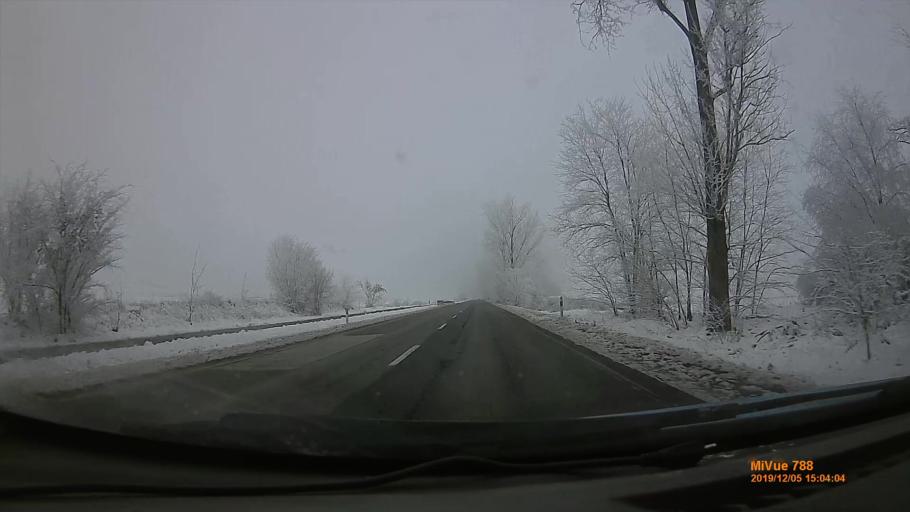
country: HU
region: Szabolcs-Szatmar-Bereg
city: Tiszanagyfalu
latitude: 48.0918
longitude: 21.4953
